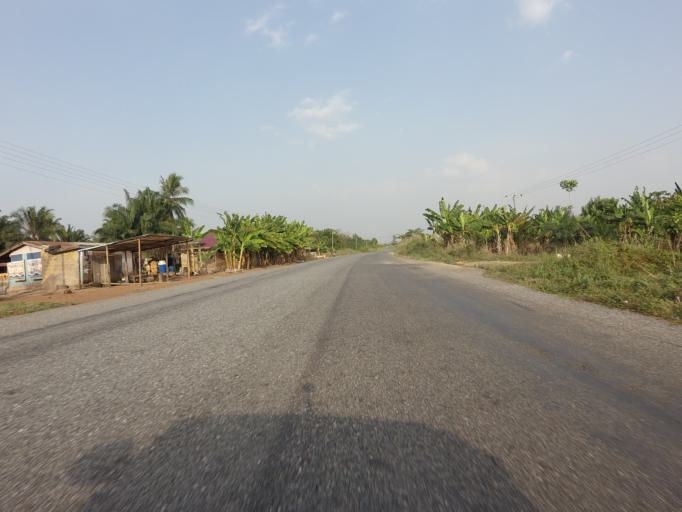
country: GH
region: Volta
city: Ho
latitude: 6.4189
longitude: 0.1786
